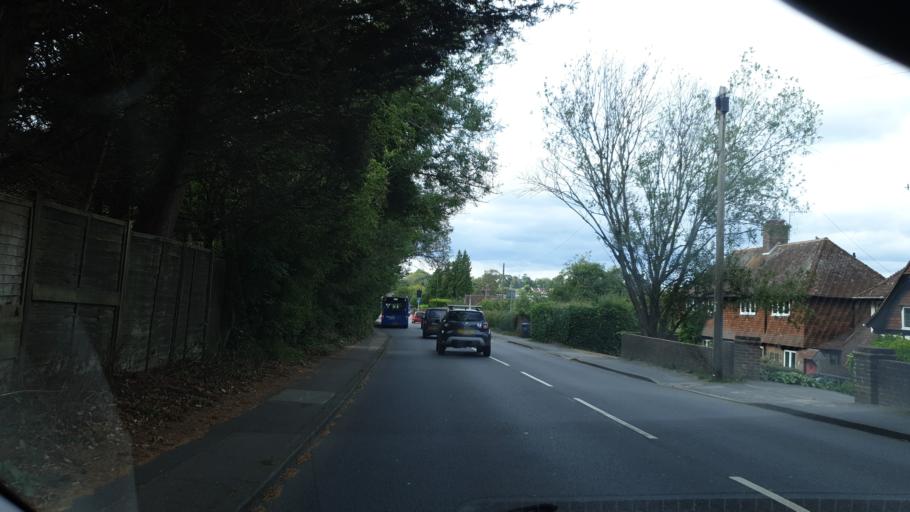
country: GB
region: England
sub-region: West Sussex
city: East Grinstead
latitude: 51.1223
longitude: 0.0053
